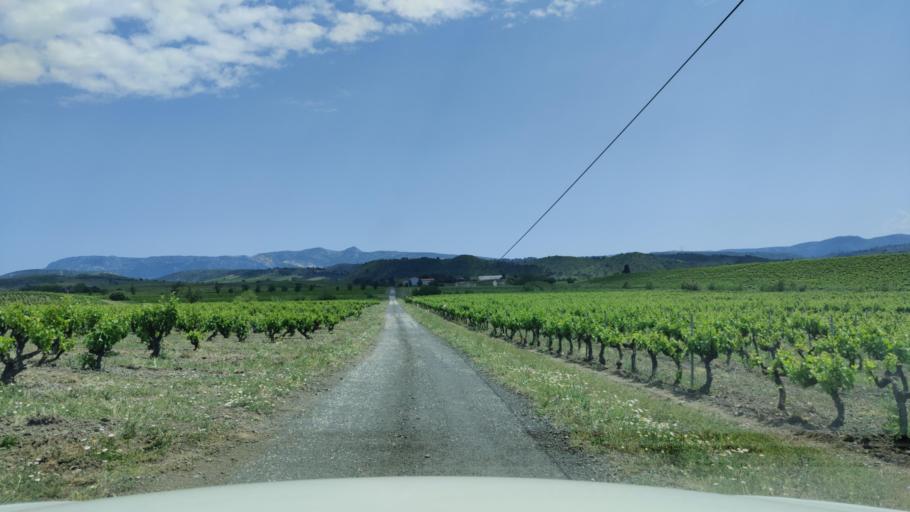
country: FR
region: Languedoc-Roussillon
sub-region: Departement des Pyrenees-Orientales
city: Estagel
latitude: 42.8161
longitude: 2.6701
